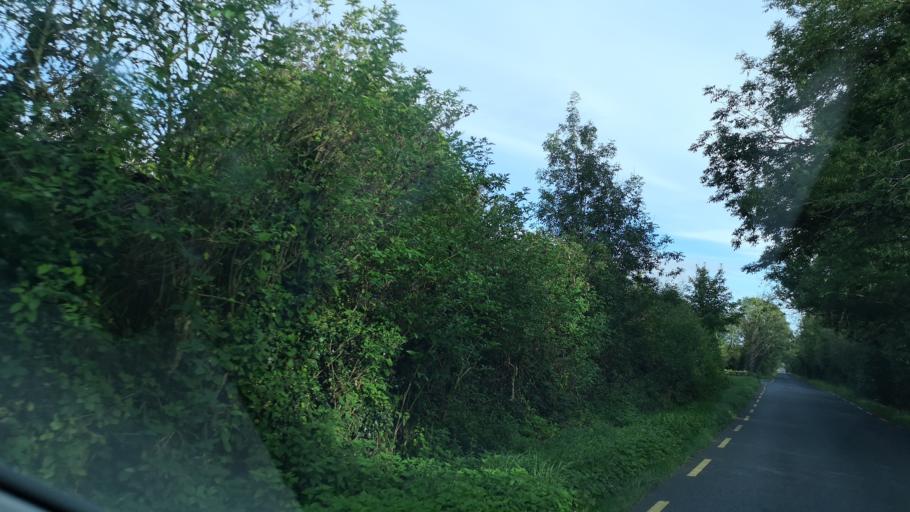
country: IE
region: Connaught
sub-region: County Galway
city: Ballinasloe
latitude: 53.3377
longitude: -8.2889
